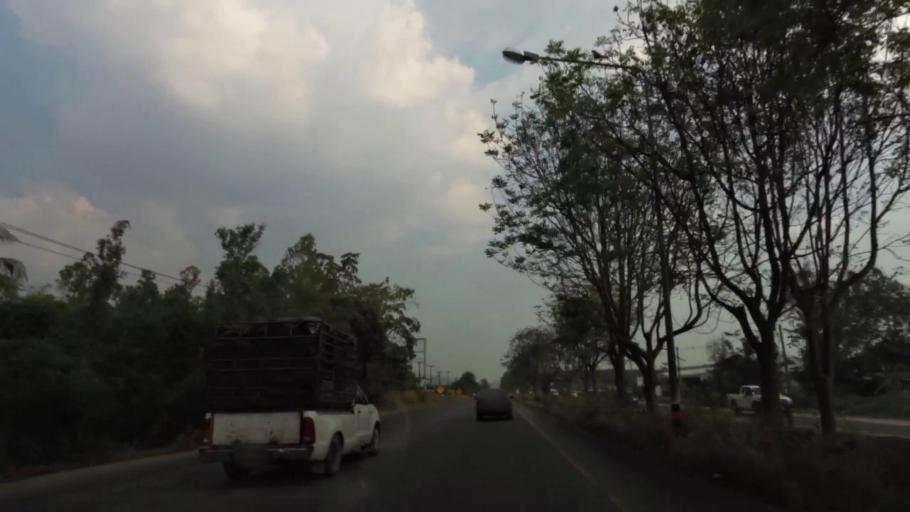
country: TH
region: Rayong
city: Wang Chan
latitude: 13.0176
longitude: 101.4616
